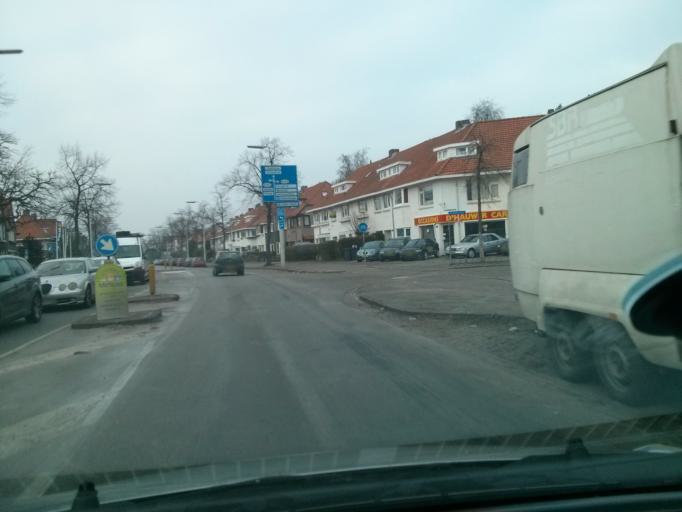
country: NL
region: North Brabant
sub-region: Gemeente Eindhoven
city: Lakerlopen
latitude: 51.4210
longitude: 5.4950
